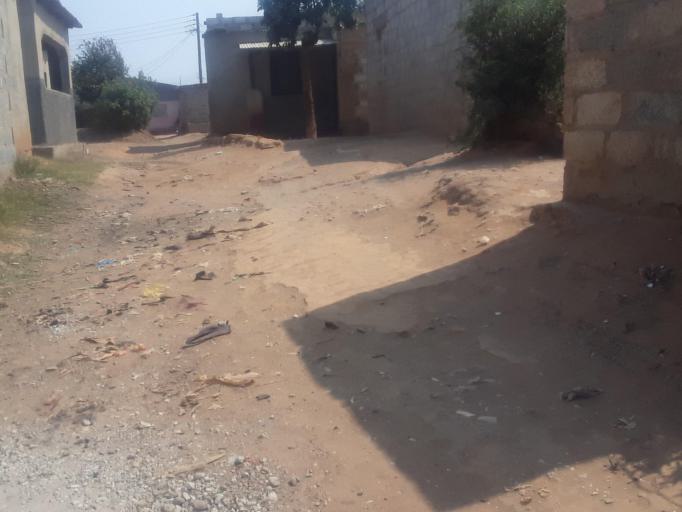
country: ZM
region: Lusaka
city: Lusaka
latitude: -15.3531
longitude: 28.2919
